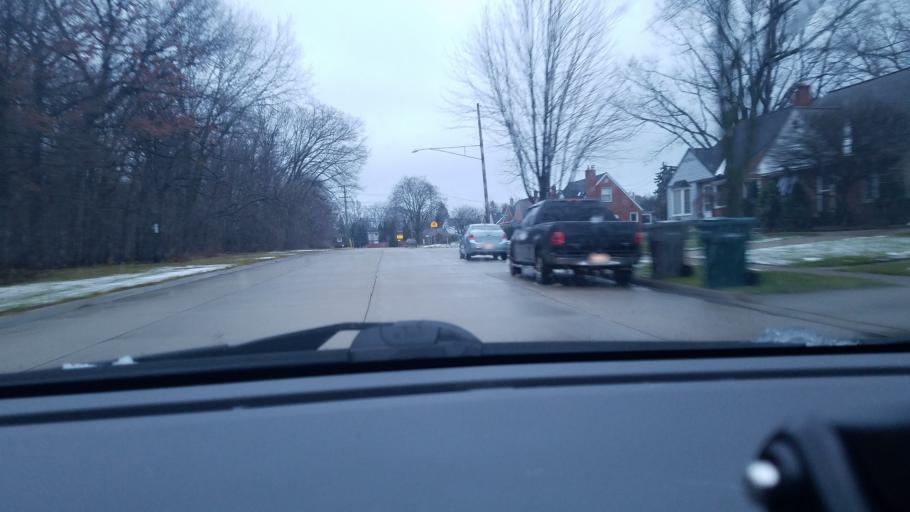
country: US
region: Michigan
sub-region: Wayne County
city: Allen Park
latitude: 42.2911
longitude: -83.2251
